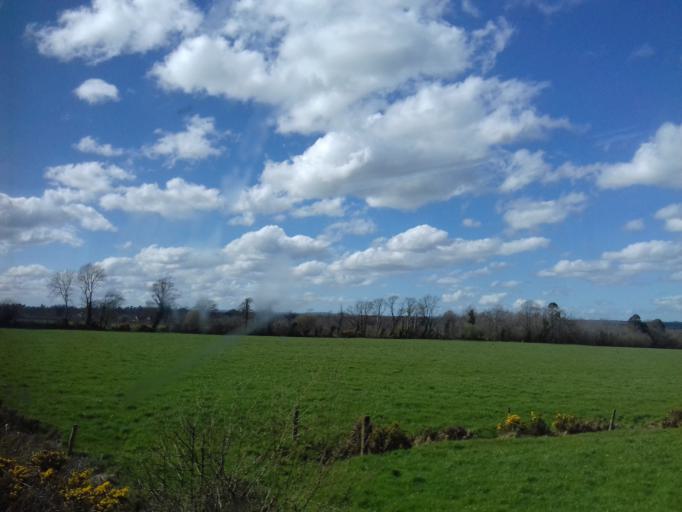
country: IE
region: Munster
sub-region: County Cork
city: Kanturk
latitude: 52.1293
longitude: -8.8363
